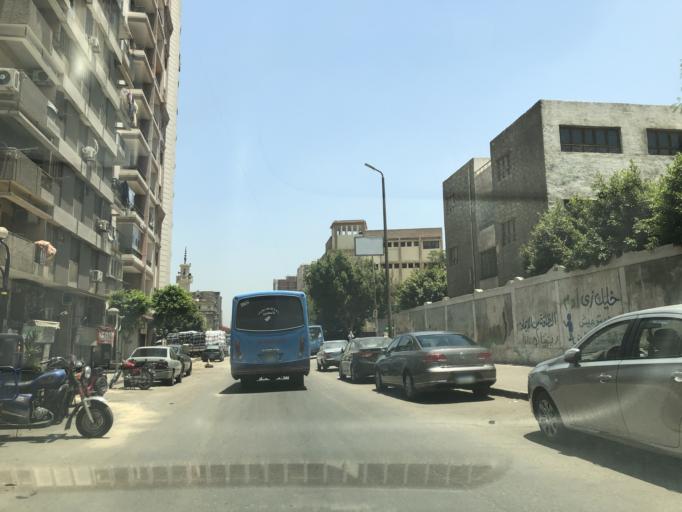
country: EG
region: Muhafazat al Qahirah
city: Cairo
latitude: 30.0640
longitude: 31.2755
